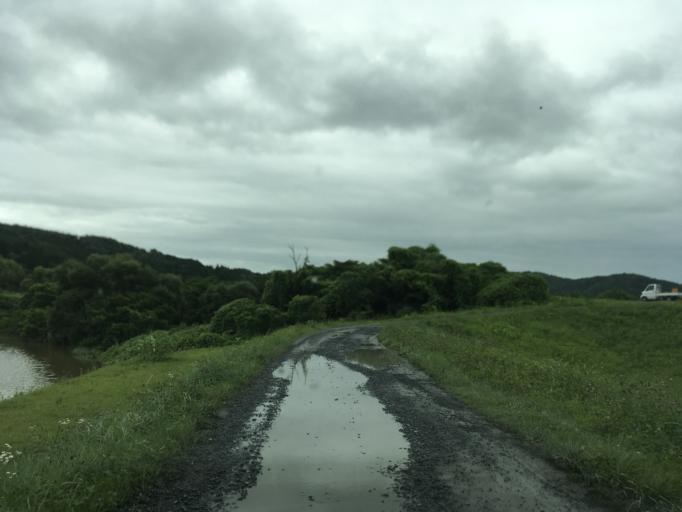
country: JP
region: Iwate
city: Ichinoseki
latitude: 38.8364
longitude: 141.2653
